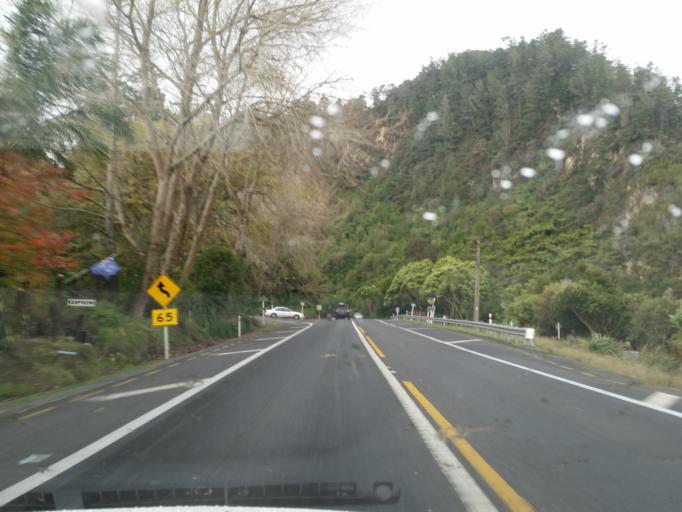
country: NZ
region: Waikato
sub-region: Hauraki District
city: Paeroa
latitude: -37.4222
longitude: 175.7212
